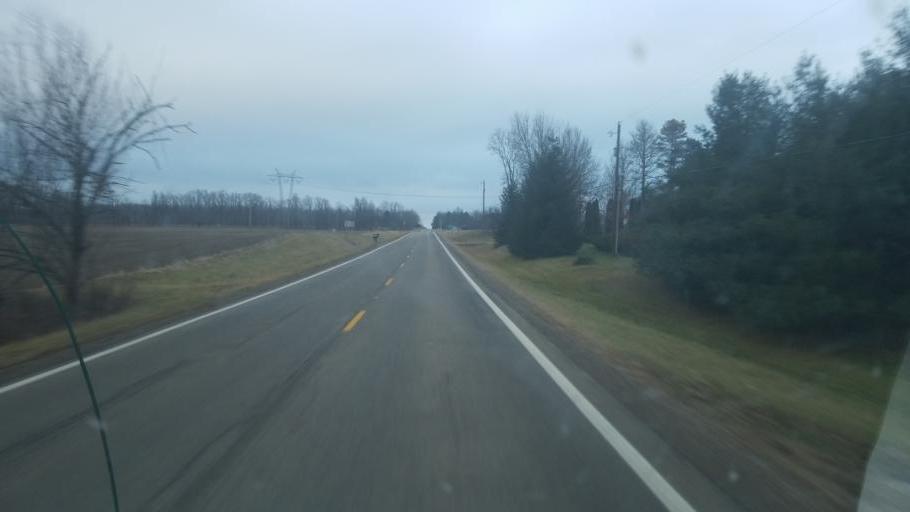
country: US
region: Ohio
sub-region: Crawford County
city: Galion
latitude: 40.6809
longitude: -82.7655
